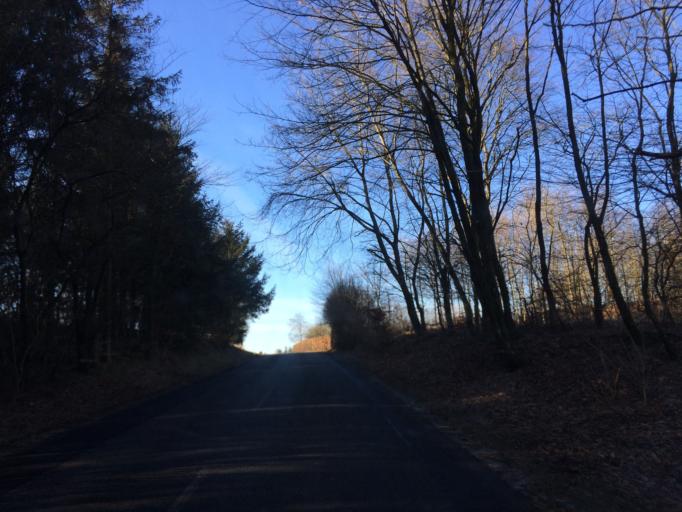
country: DK
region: North Denmark
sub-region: Mariagerfjord Kommune
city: Hobro
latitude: 56.6089
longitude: 9.6365
